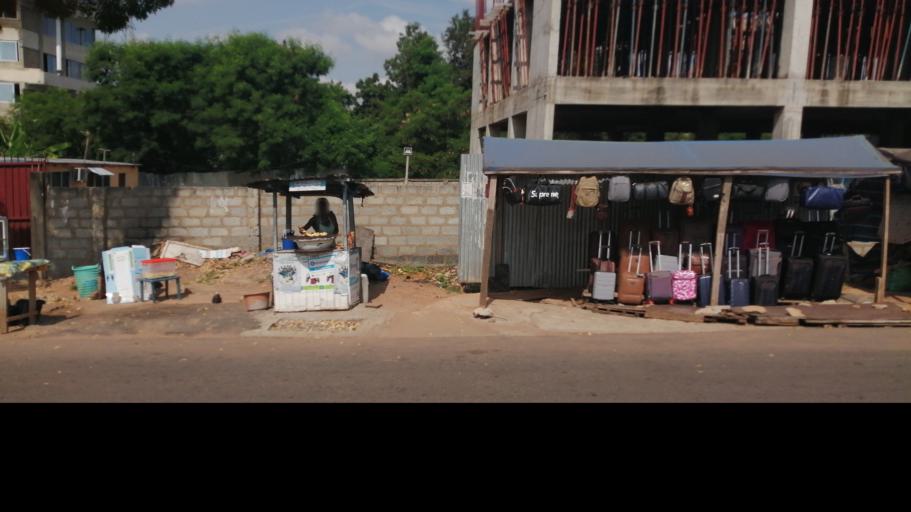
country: GH
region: Greater Accra
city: Medina Estates
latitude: 5.6389
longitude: -0.1707
